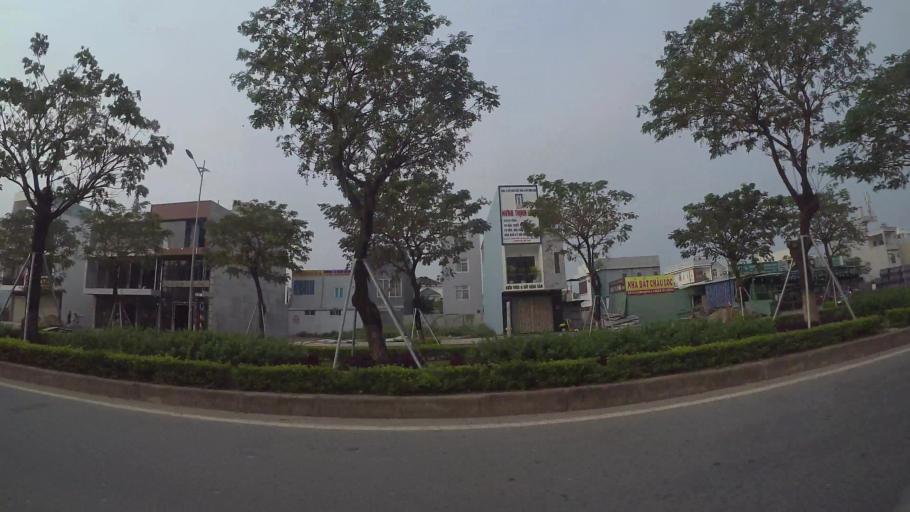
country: VN
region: Da Nang
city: Ngu Hanh Son
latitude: 16.0196
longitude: 108.2290
